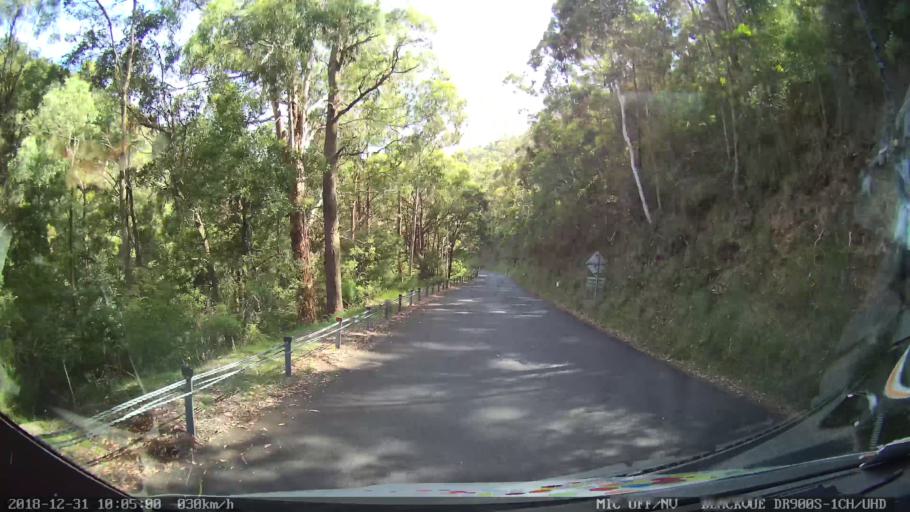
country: AU
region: New South Wales
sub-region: Snowy River
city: Jindabyne
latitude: -36.5285
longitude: 148.1933
